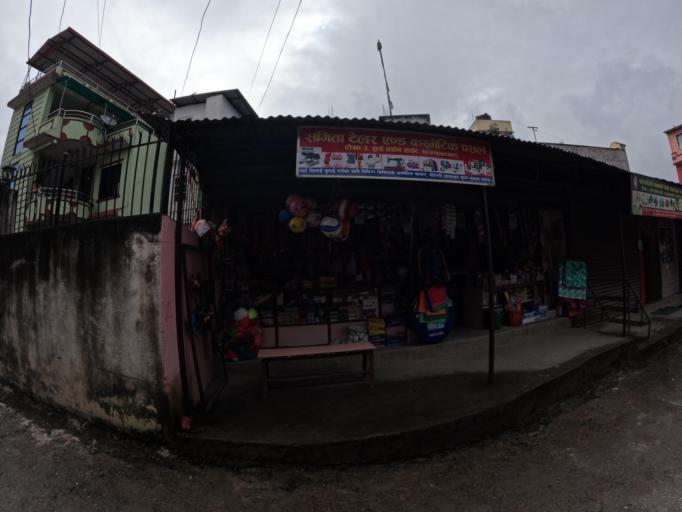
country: NP
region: Central Region
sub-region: Bagmati Zone
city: Kathmandu
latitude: 27.7575
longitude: 85.3225
